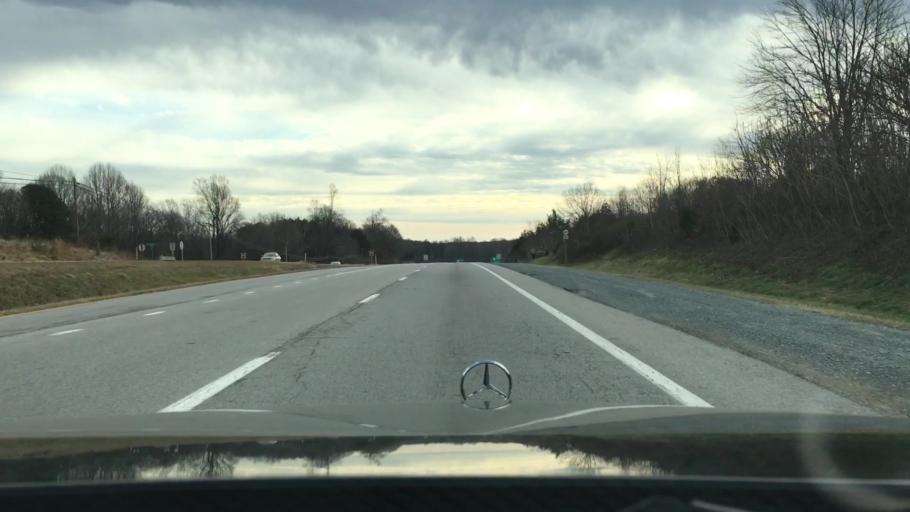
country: US
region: Virginia
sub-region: Pittsylvania County
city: Gretna
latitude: 36.9852
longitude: -79.3549
